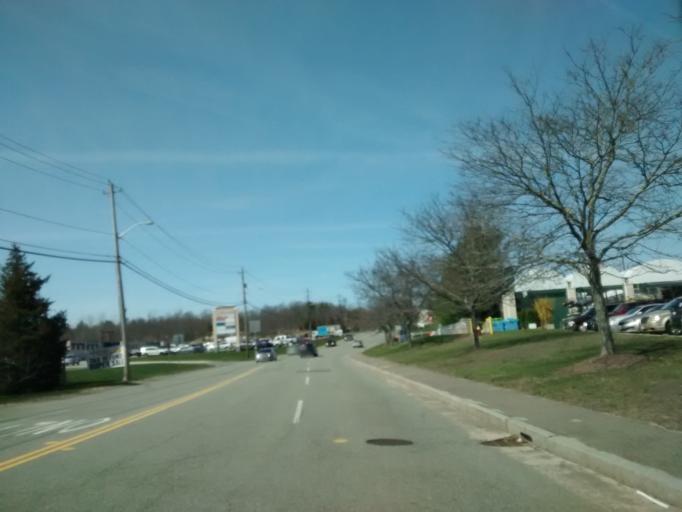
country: US
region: Massachusetts
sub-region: Norfolk County
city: Avon
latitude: 42.1302
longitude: -71.0666
